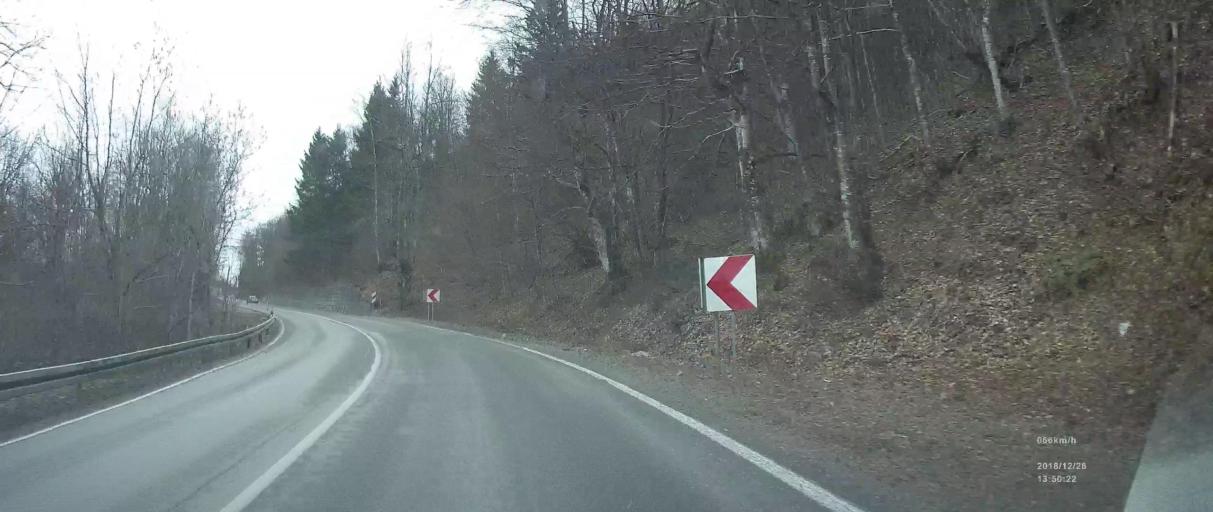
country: HR
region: Primorsko-Goranska
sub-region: Grad Delnice
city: Delnice
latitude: 45.3946
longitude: 14.8294
